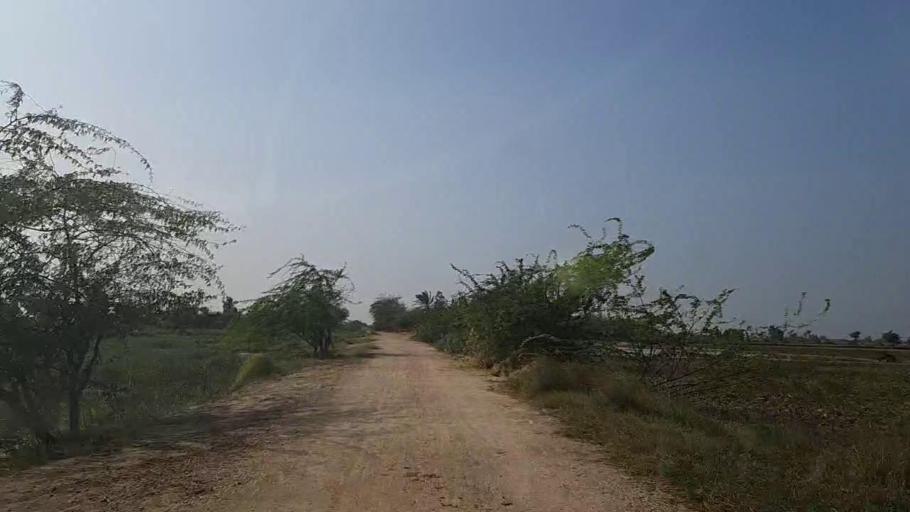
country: PK
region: Sindh
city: Mirpur Sakro
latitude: 24.5677
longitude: 67.8197
